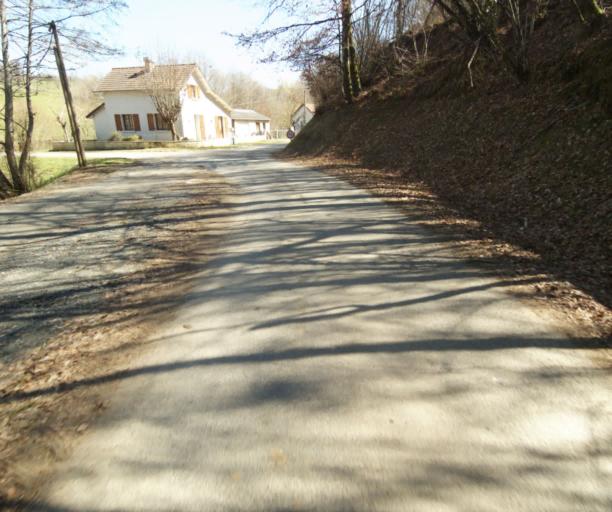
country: FR
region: Limousin
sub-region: Departement de la Correze
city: Saint-Clement
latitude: 45.3956
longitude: 1.6503
